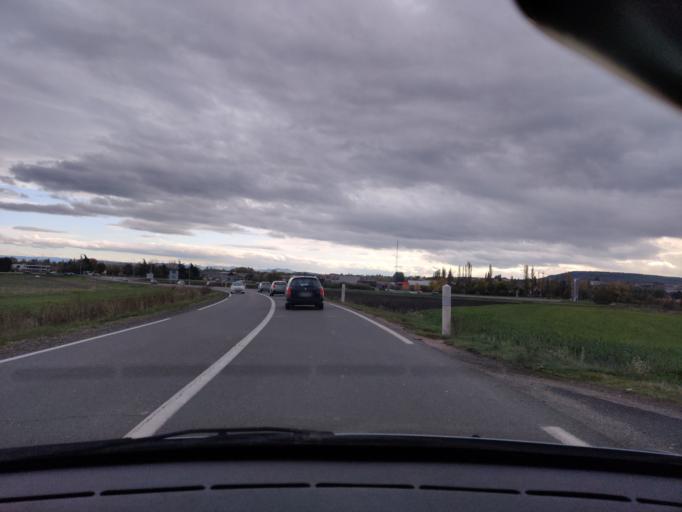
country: FR
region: Auvergne
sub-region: Departement du Puy-de-Dome
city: Riom
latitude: 45.9099
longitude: 3.1217
